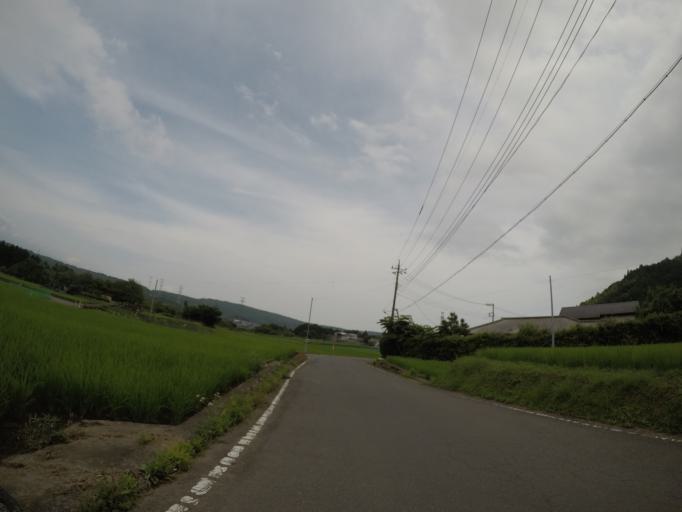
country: JP
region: Shizuoka
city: Fujinomiya
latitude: 35.2493
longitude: 138.5535
